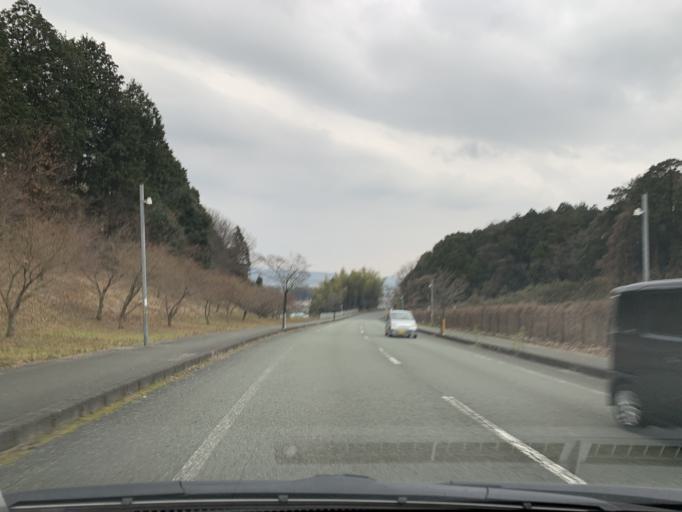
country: JP
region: Kumamoto
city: Ozu
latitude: 32.8840
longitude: 130.8829
